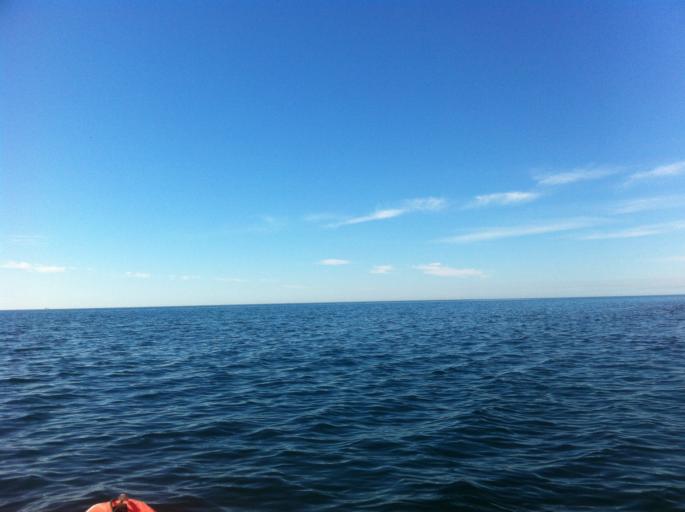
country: MX
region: Sonora
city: Heroica Guaymas
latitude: 27.9086
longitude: -110.9690
